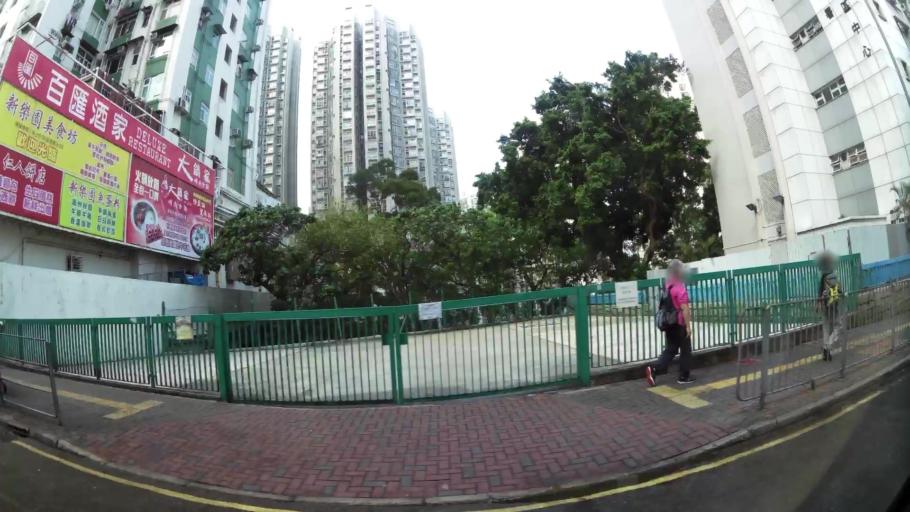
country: HK
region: Kowloon City
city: Kowloon
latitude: 22.3088
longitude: 114.2342
